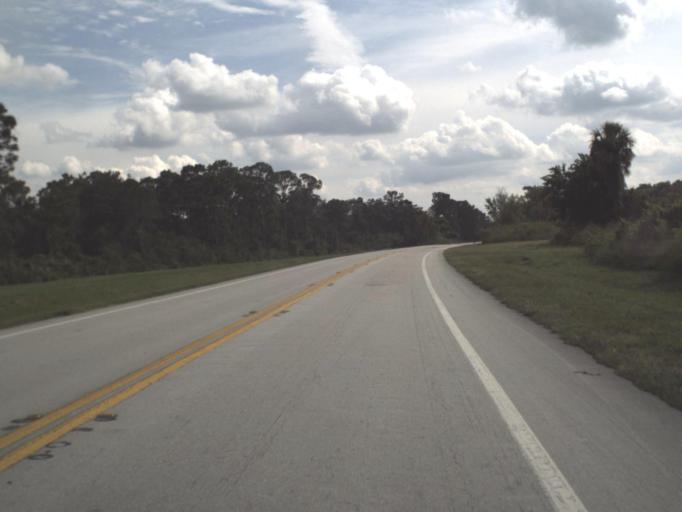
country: US
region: Florida
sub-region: Indian River County
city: Fellsmere
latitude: 27.5797
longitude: -80.8351
